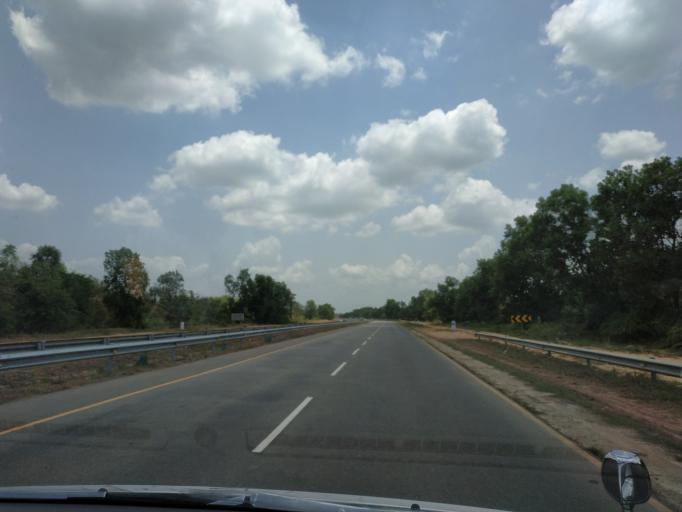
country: MM
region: Bago
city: Thanatpin
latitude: 17.2924
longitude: 96.2288
